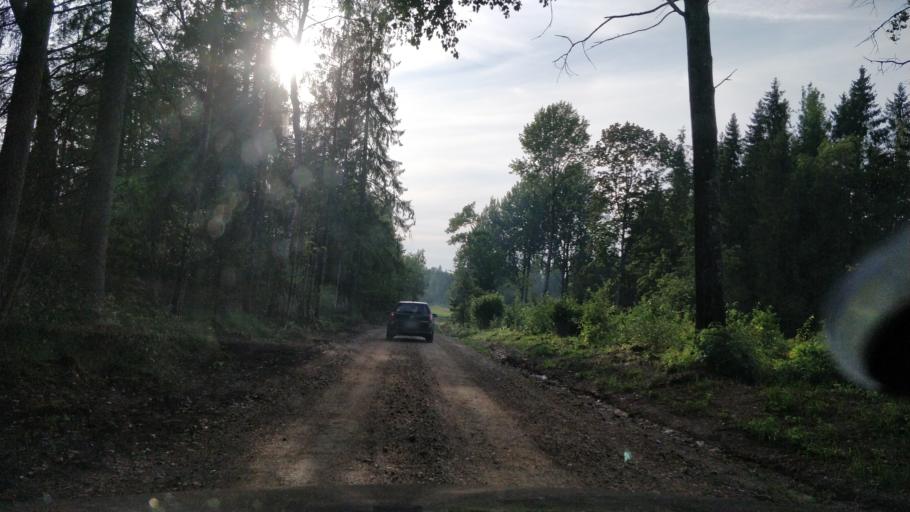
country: LV
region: Sigulda
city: Sigulda
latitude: 57.1001
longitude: 24.7924
